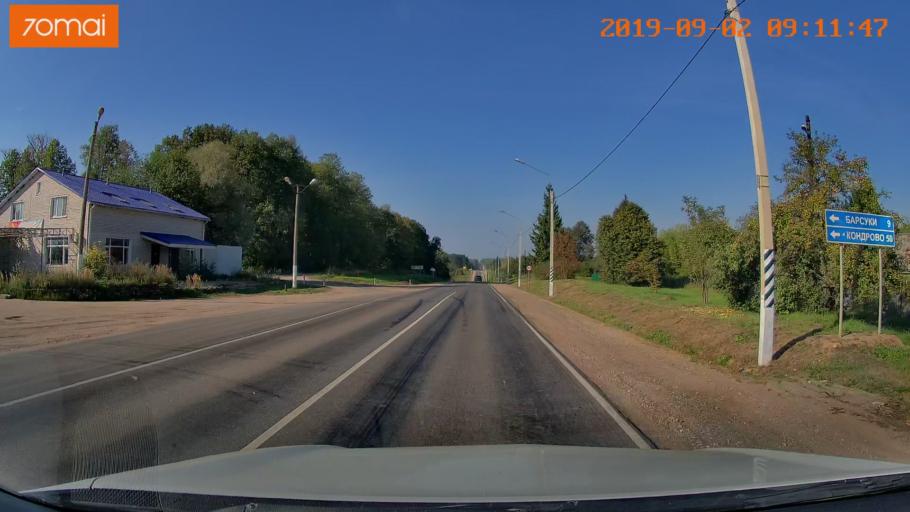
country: RU
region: Kaluga
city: Myatlevo
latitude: 54.8649
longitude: 35.5682
